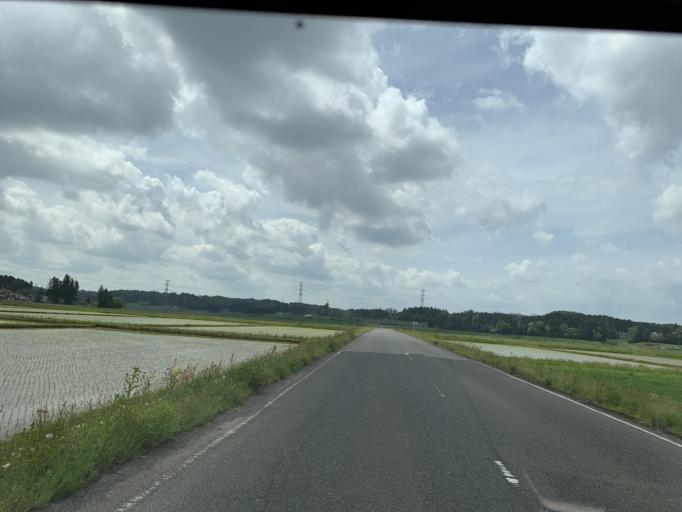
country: JP
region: Iwate
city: Ichinoseki
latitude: 38.8238
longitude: 141.0204
